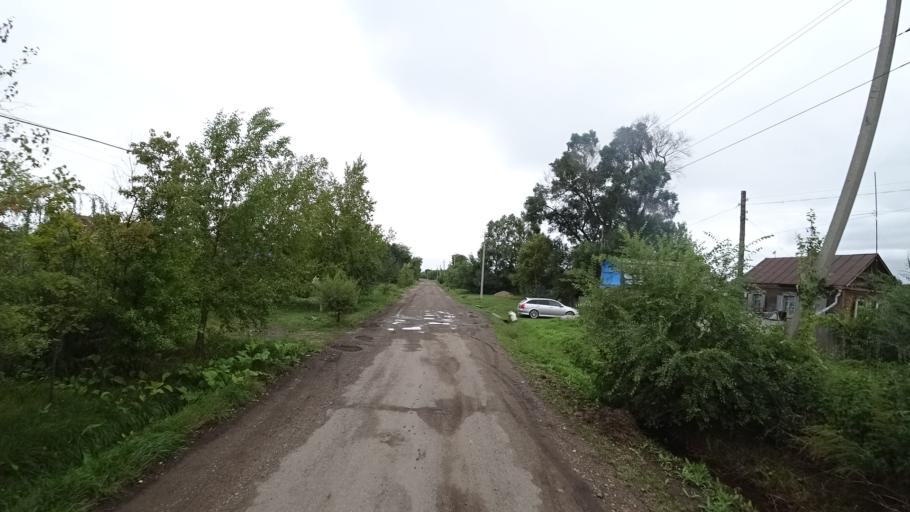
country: RU
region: Primorskiy
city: Chernigovka
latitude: 44.3485
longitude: 132.5757
